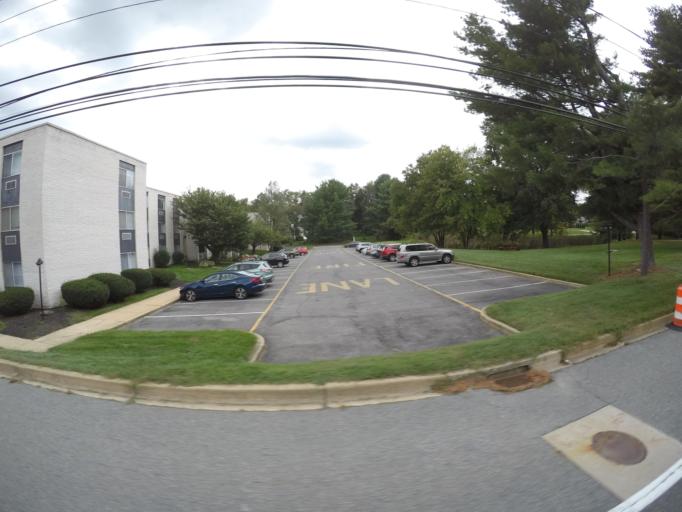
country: US
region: Delaware
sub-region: New Castle County
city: Newark
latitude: 39.6963
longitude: -75.7652
